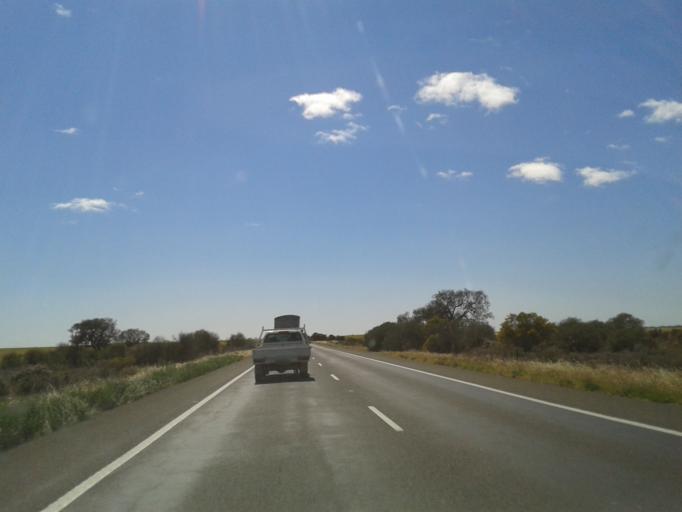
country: AU
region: New South Wales
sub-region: Wentworth
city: Dareton
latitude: -34.2400
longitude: 141.9619
